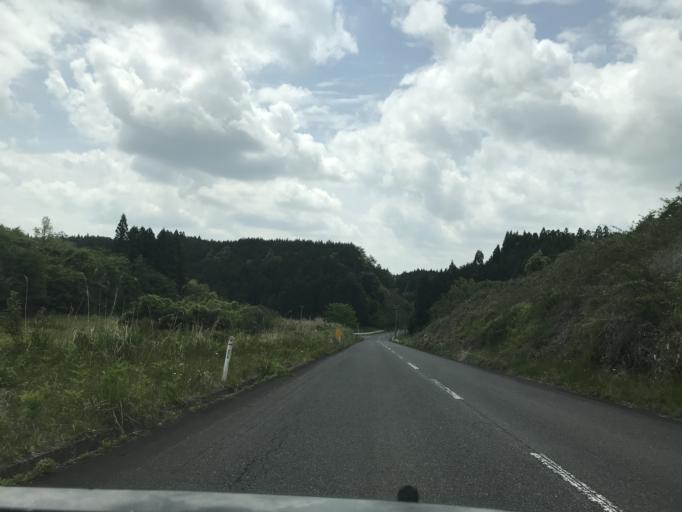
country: JP
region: Miyagi
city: Furukawa
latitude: 38.7163
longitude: 140.9203
